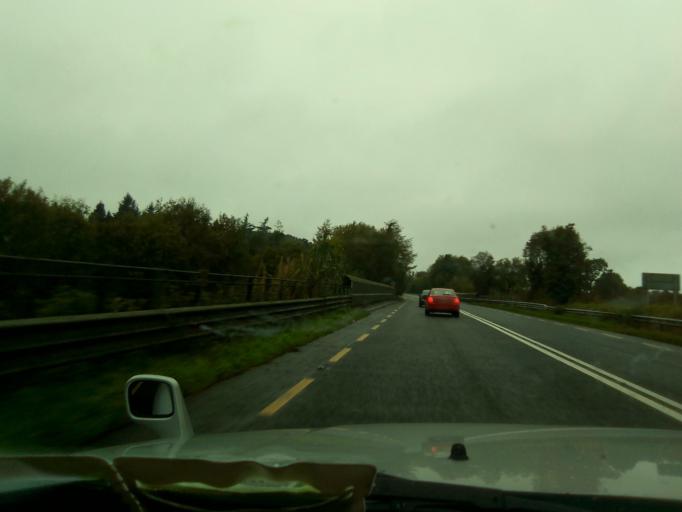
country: IE
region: Leinster
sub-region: An Iarmhi
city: An Muileann gCearr
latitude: 53.5995
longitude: -7.3948
